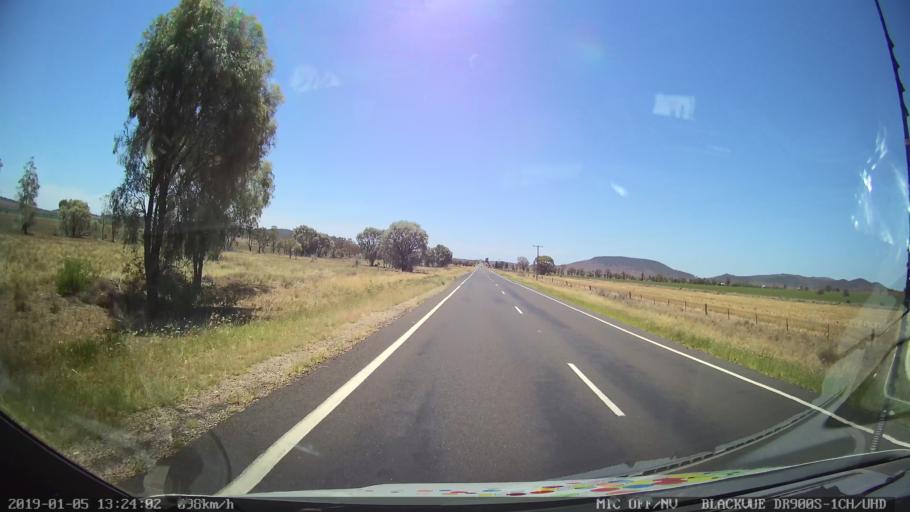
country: AU
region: New South Wales
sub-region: Gunnedah
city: Gunnedah
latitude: -31.0730
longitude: 149.9833
